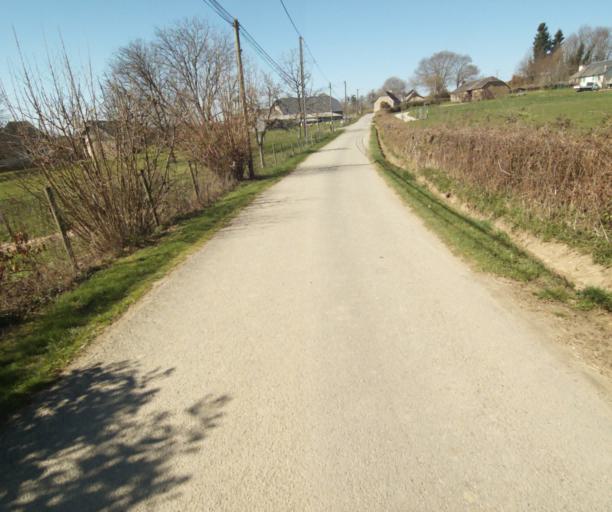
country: FR
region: Limousin
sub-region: Departement de la Correze
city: Saint-Mexant
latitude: 45.2992
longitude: 1.6187
